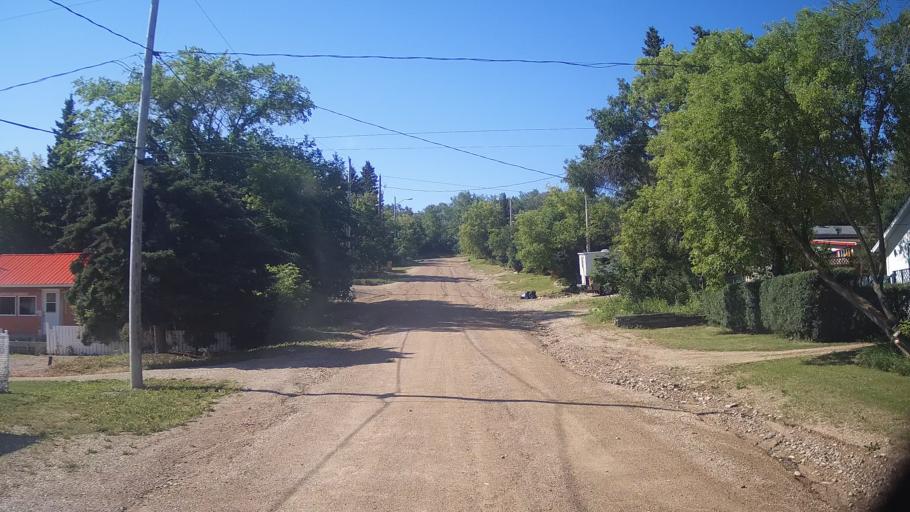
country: CA
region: Saskatchewan
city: Watrous
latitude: 51.7210
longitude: -105.4490
